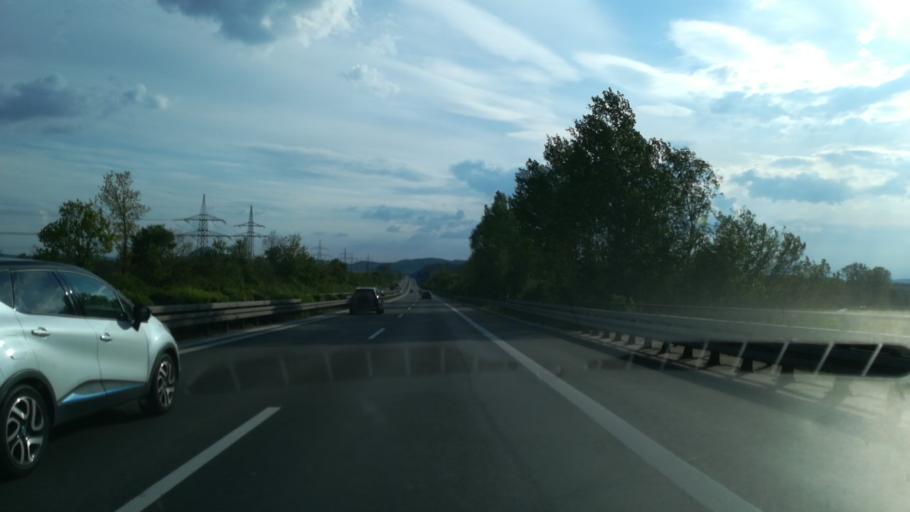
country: DE
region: Baden-Wuerttemberg
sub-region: Freiburg Region
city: Volkertshausen
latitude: 47.8215
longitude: 8.8892
